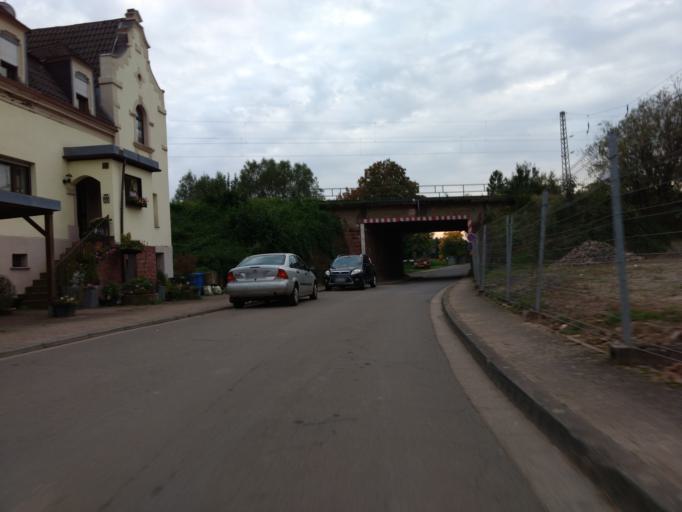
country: DE
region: Saarland
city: Beckingen
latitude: 49.3869
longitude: 6.6944
